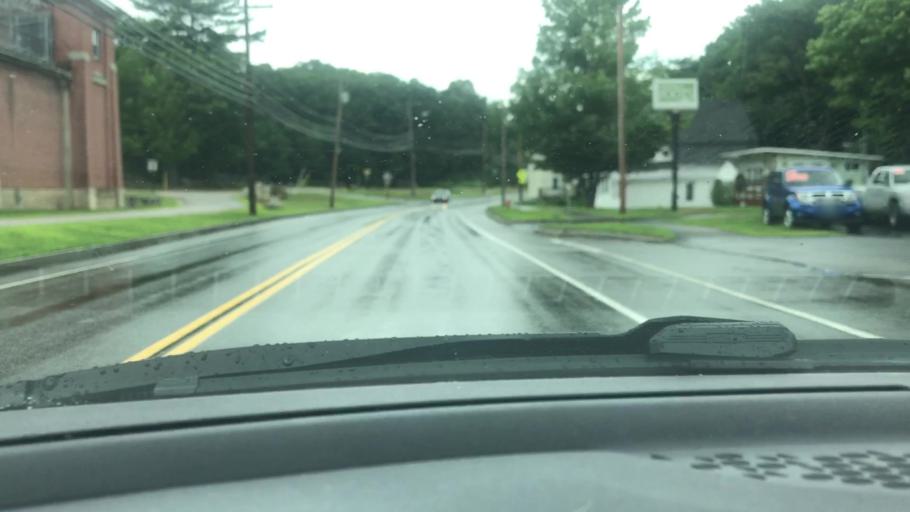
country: US
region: New Hampshire
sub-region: Merrimack County
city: East Concord
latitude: 43.2285
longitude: -71.5580
